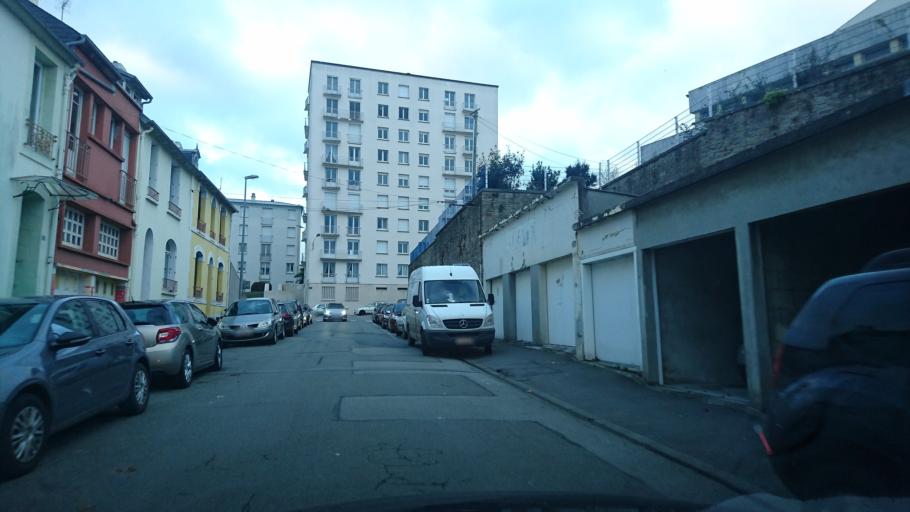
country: FR
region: Brittany
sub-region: Departement du Finistere
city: Brest
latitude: 48.3896
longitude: -4.4793
